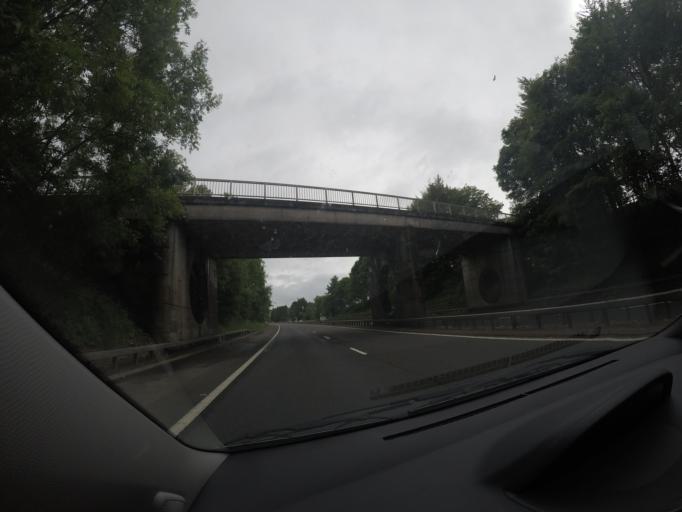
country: GB
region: Scotland
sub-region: Falkirk
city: Dunipace
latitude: 56.0149
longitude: -3.9213
